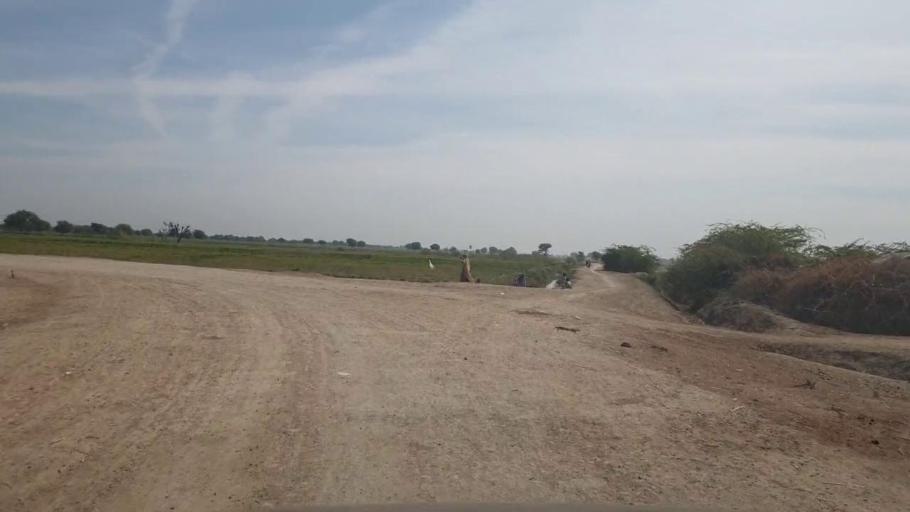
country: PK
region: Sindh
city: Umarkot
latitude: 25.3300
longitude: 69.6154
